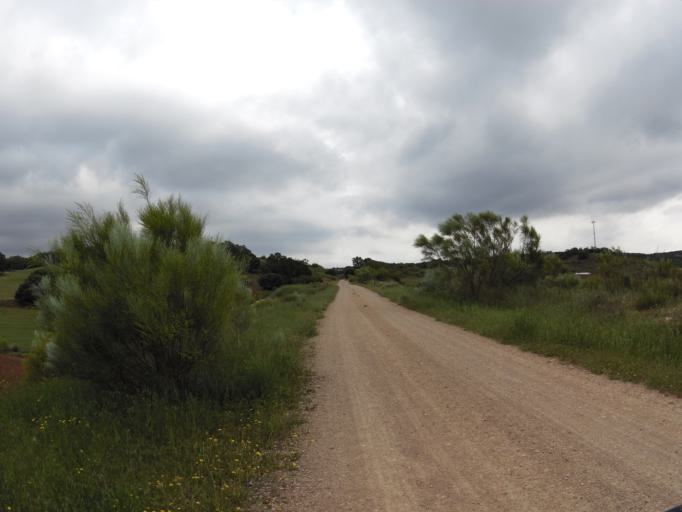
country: ES
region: Castille-La Mancha
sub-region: Provincia de Albacete
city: Robledo
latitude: 38.7282
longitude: -2.4758
